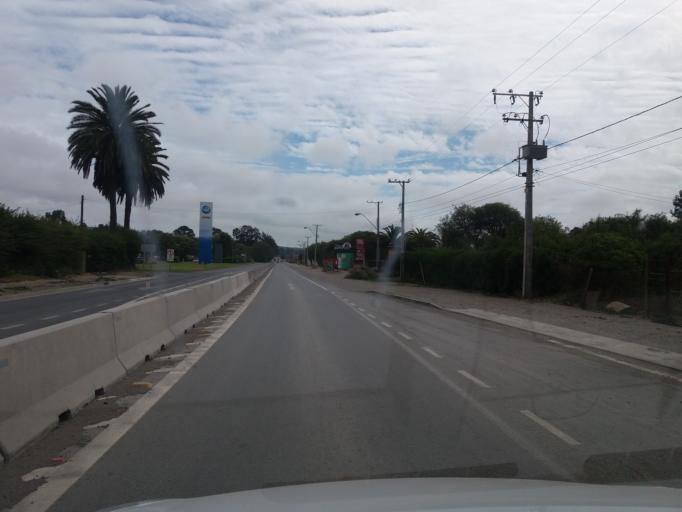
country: CL
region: Valparaiso
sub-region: Provincia de Marga Marga
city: Quilpue
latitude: -32.9281
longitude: -71.4250
